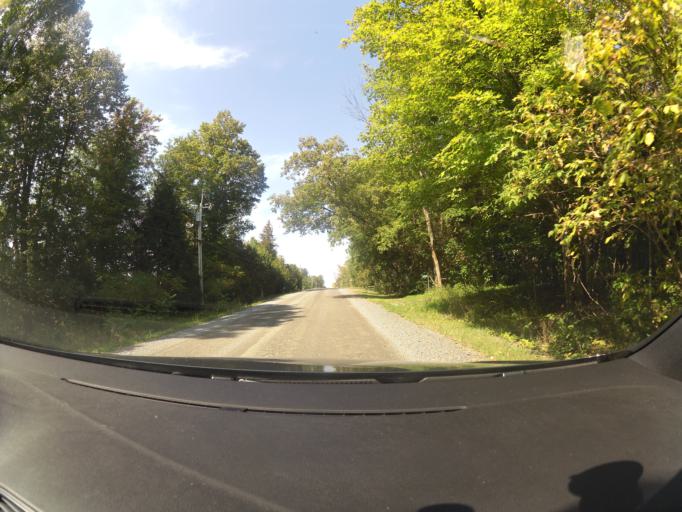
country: CA
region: Ontario
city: Arnprior
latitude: 45.3362
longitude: -76.1883
